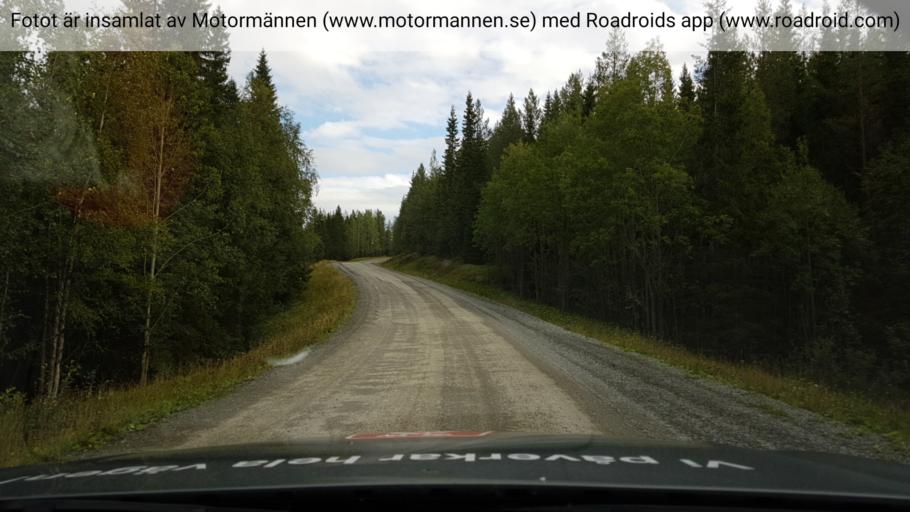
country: SE
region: Jaemtland
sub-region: Krokoms Kommun
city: Valla
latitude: 63.6755
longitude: 13.6910
